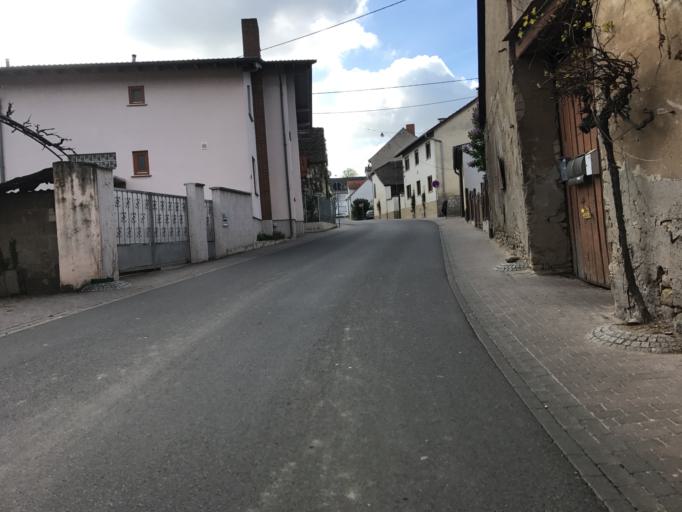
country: DE
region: Rheinland-Pfalz
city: Bubenheim
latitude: 49.9208
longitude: 8.0800
